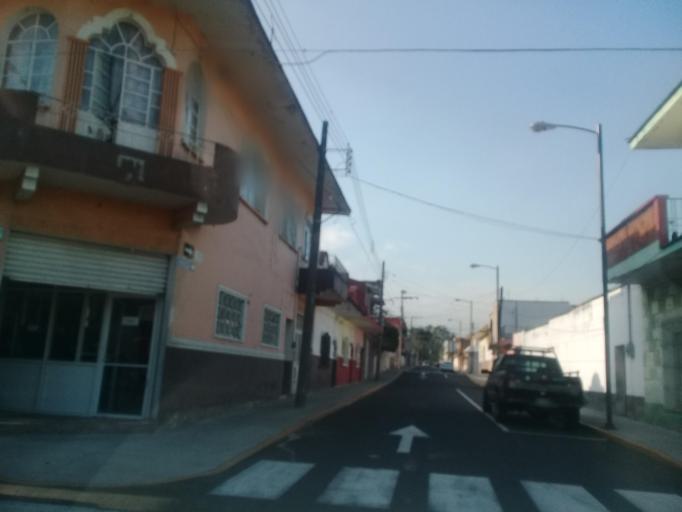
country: MX
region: Veracruz
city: Orizaba
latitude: 18.8511
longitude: -97.1121
